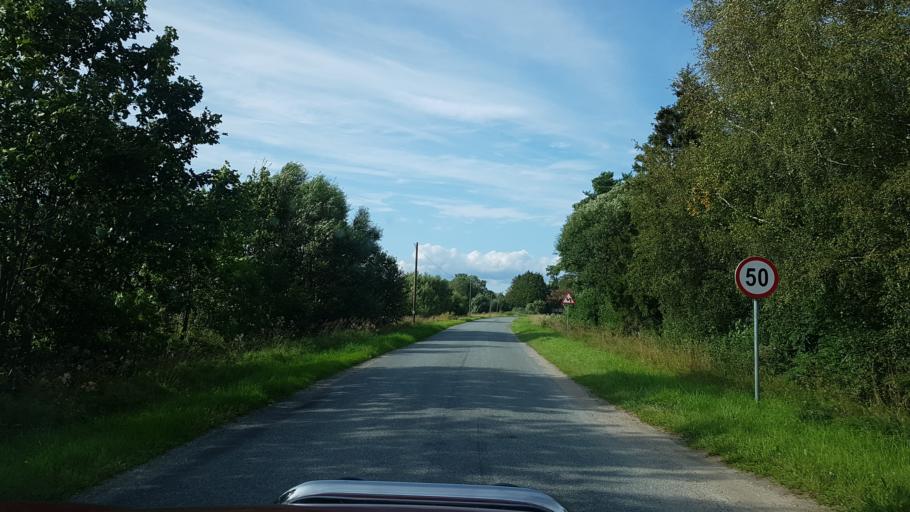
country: EE
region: Laeaene
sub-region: Lihula vald
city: Lihula
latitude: 58.4409
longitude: 24.0040
